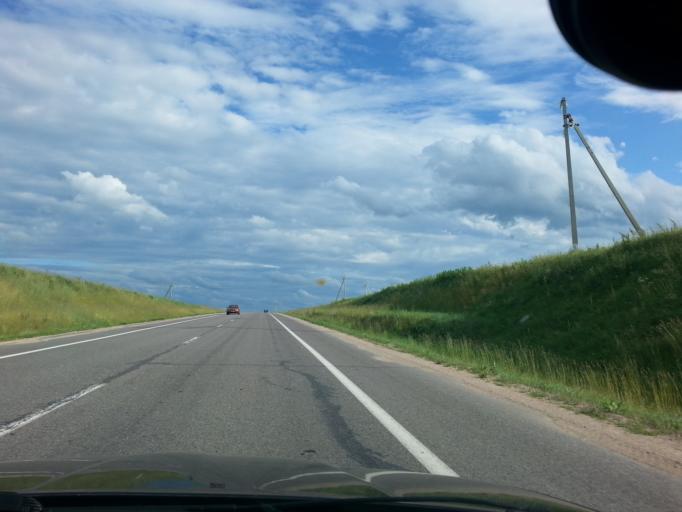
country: BY
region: Grodnenskaya
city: Astravyets
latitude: 54.7769
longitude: 26.0562
